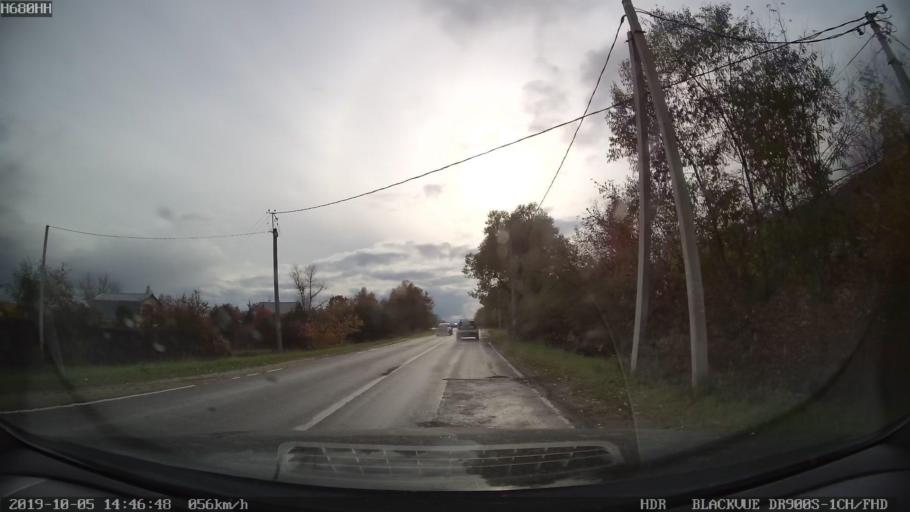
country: RU
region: Moskovskaya
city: Solnechnogorsk
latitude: 56.2240
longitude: 36.9064
